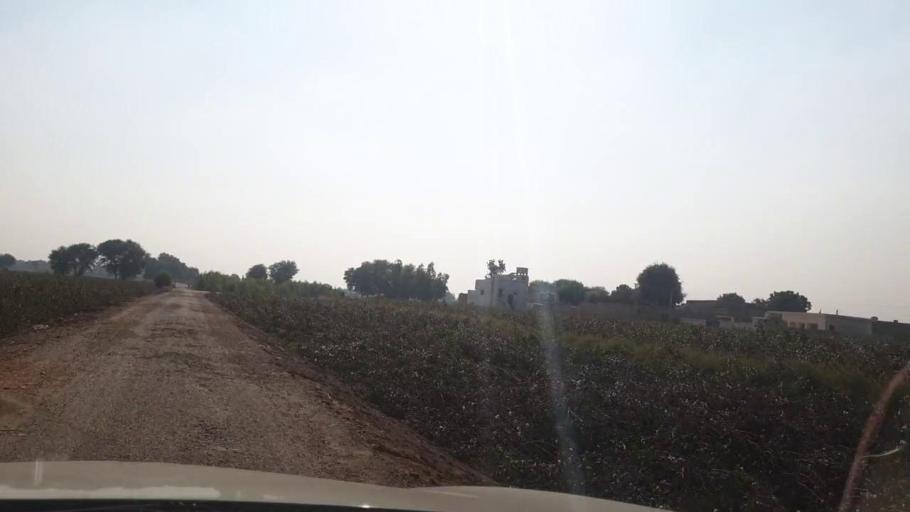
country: PK
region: Sindh
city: Bhan
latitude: 26.5302
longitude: 67.7435
